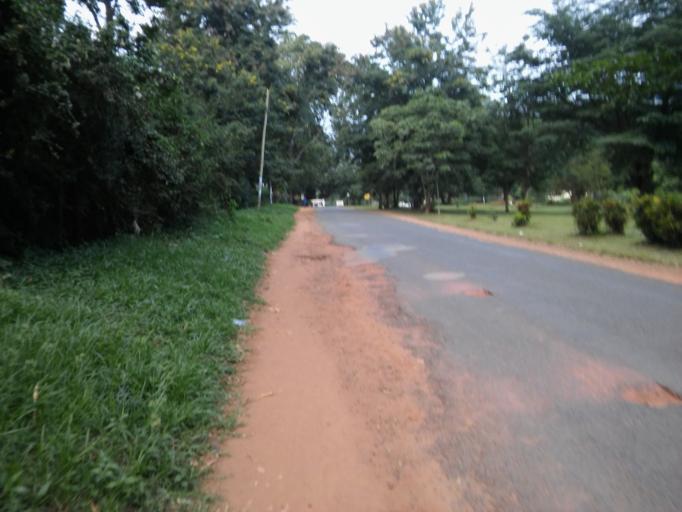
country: UG
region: Eastern Region
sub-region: Mbale District
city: Mbale
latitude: 1.0667
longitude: 34.1920
